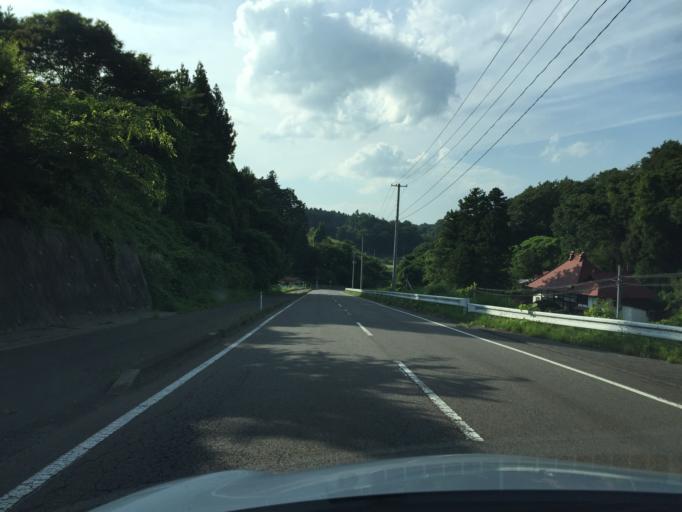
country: JP
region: Fukushima
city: Miharu
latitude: 37.4102
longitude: 140.5004
